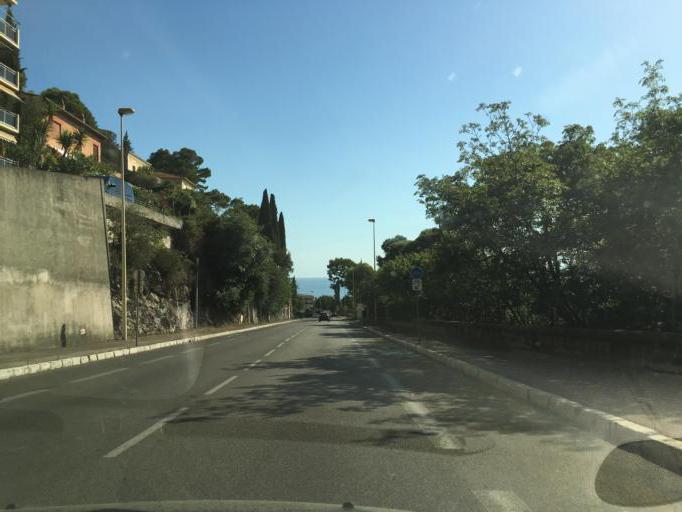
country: FR
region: Provence-Alpes-Cote d'Azur
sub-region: Departement des Alpes-Maritimes
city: Villefranche-sur-Mer
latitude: 43.7018
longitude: 7.2974
